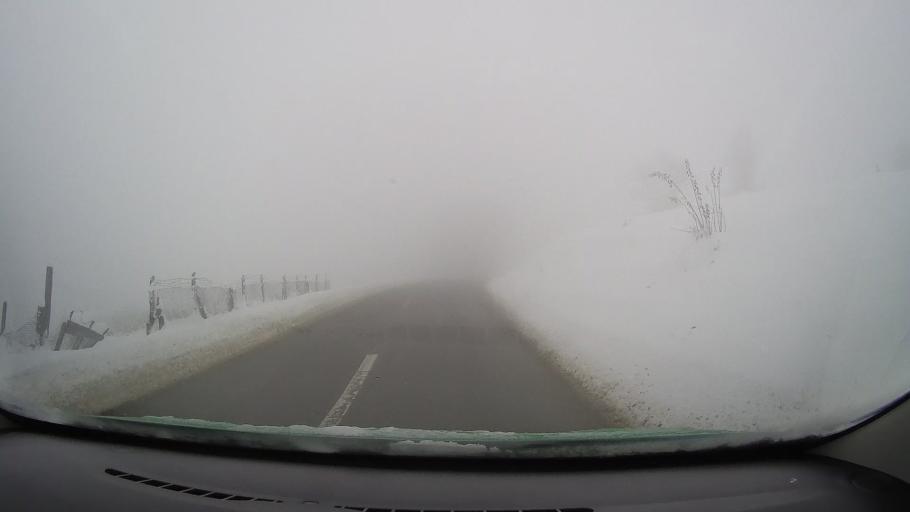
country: RO
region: Sibiu
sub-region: Comuna Poiana Sibiului
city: Poiana Sibiului
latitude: 45.8097
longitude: 23.7448
